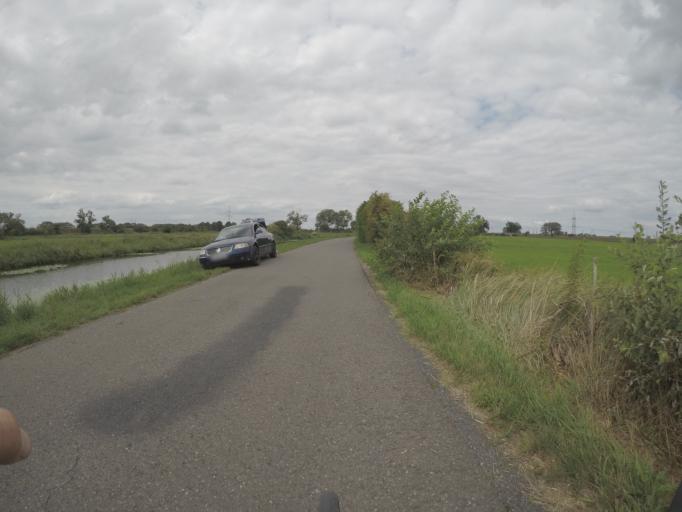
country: DE
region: Brandenburg
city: Wustermark
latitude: 52.5957
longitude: 12.9353
